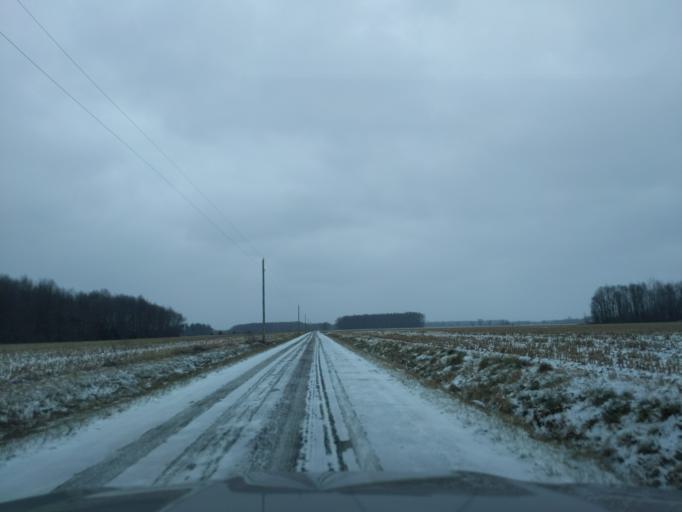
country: US
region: Indiana
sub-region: Decatur County
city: Westport
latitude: 39.2048
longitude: -85.4738
